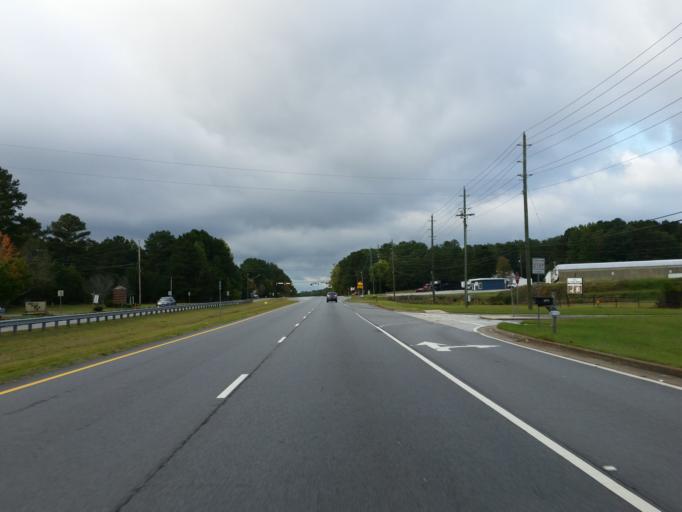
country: US
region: Georgia
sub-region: Cobb County
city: Acworth
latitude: 34.0750
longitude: -84.7273
